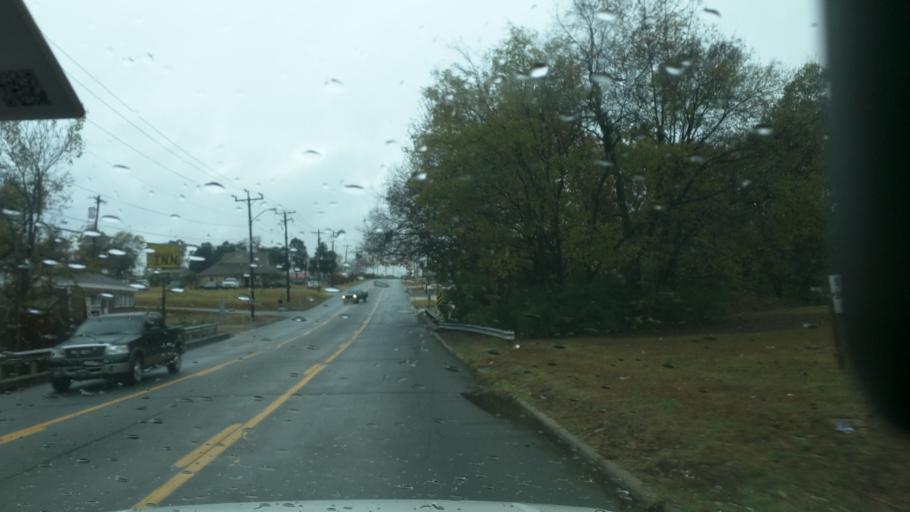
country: US
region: Arkansas
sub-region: Franklin County
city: Ozark
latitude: 35.4880
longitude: -93.8359
